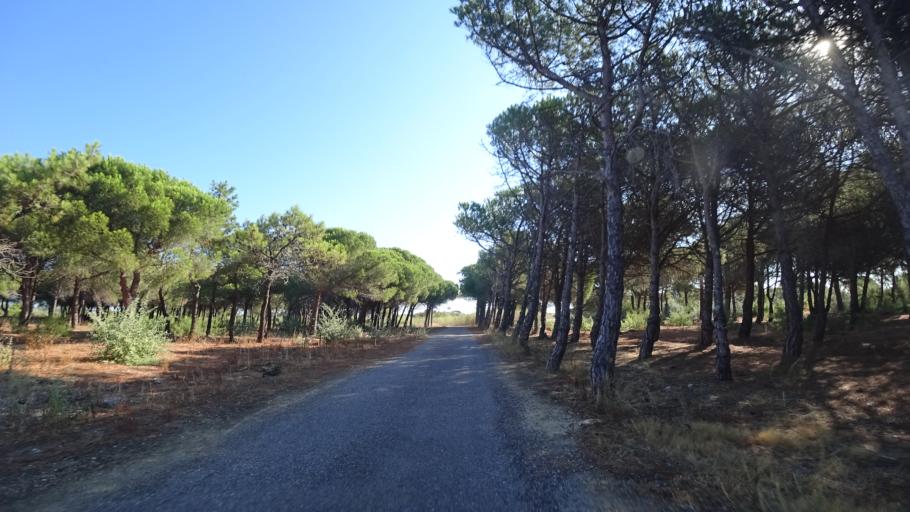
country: FR
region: Languedoc-Roussillon
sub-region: Departement de l'Aude
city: Leucate
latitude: 42.8716
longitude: 3.0370
